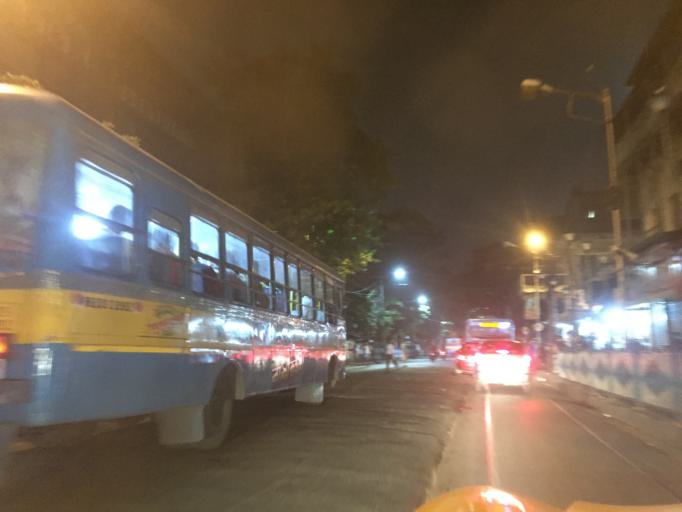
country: IN
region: West Bengal
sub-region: Kolkata
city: Bara Bazar
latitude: 22.5638
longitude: 88.3555
